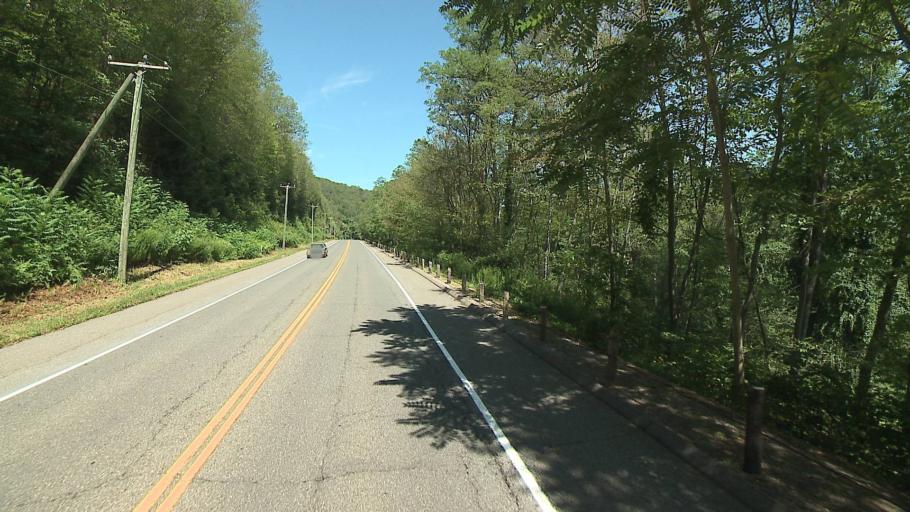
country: US
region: Connecticut
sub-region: Hartford County
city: Collinsville
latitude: 41.7977
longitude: -72.9263
